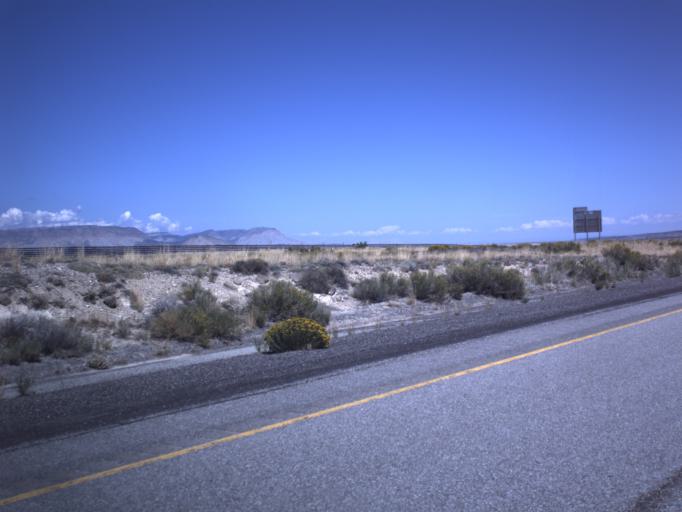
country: US
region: Utah
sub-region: Emery County
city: Ferron
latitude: 38.7701
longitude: -111.3363
